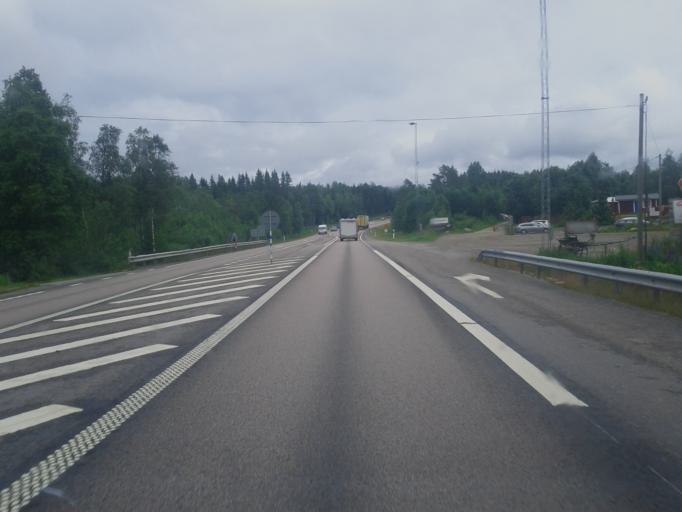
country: SE
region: Vaesternorrland
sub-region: Timra Kommun
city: Soraker
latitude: 62.5557
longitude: 17.6419
